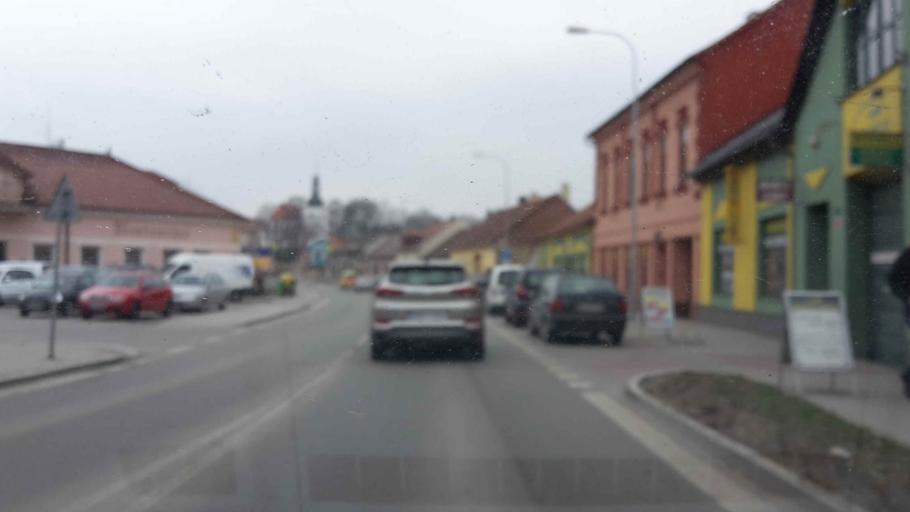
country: CZ
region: South Moravian
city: Kurim
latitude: 49.2984
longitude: 16.5298
